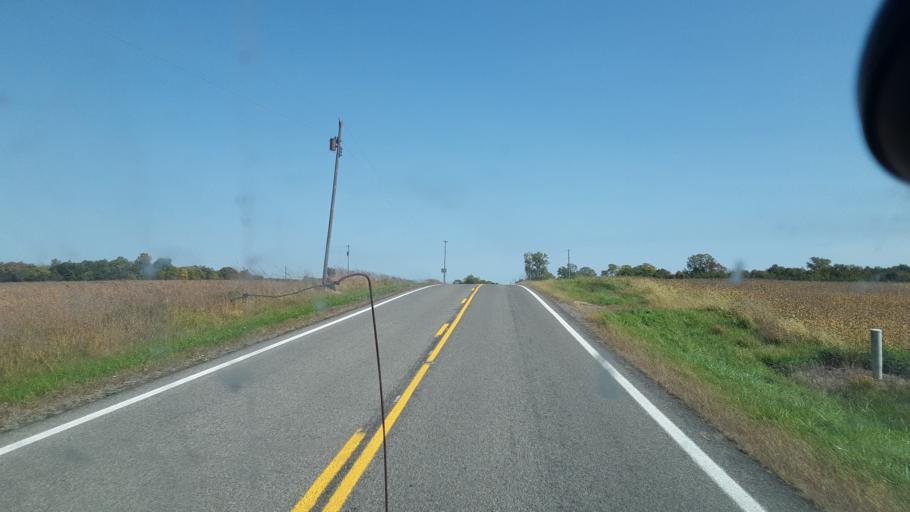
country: US
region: Ohio
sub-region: Logan County
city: Northwood
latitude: 40.5055
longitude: -83.6797
